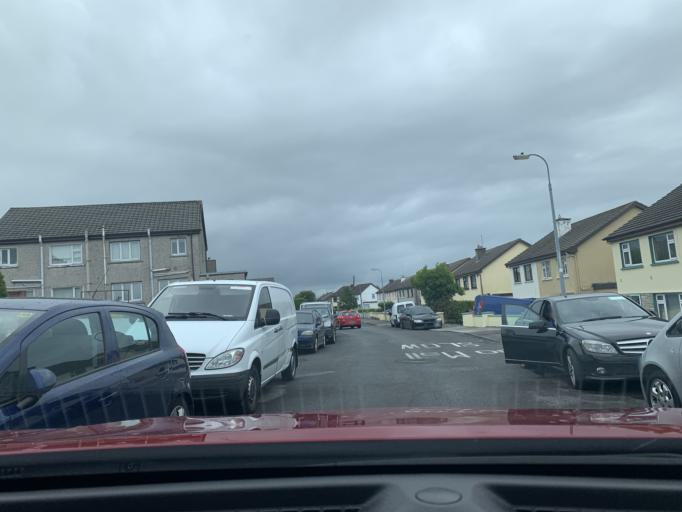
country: IE
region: Connaught
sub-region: Sligo
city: Sligo
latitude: 54.2795
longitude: -8.4826
